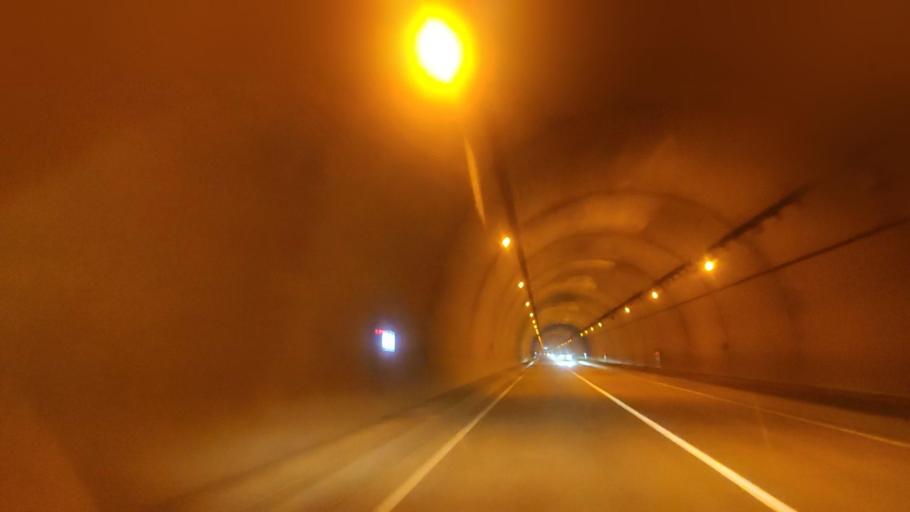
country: JP
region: Hokkaido
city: Date
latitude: 42.5636
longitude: 140.7853
